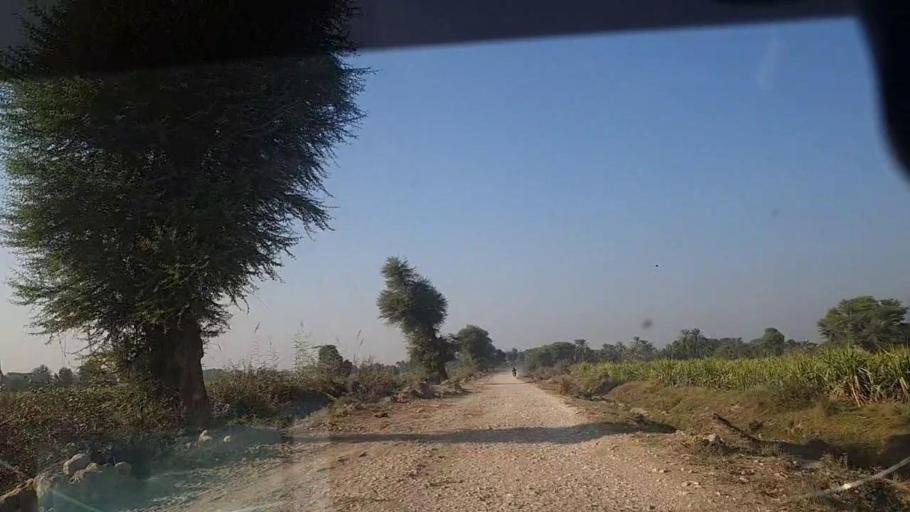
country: PK
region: Sindh
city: Sobhadero
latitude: 27.2645
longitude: 68.3496
